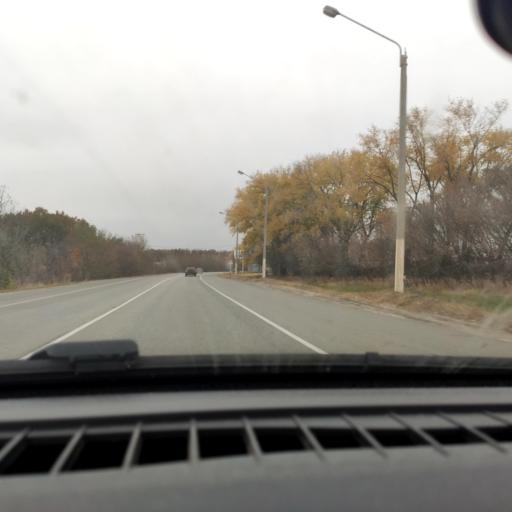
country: RU
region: Voronezj
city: Devitsa
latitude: 51.5970
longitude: 38.9752
